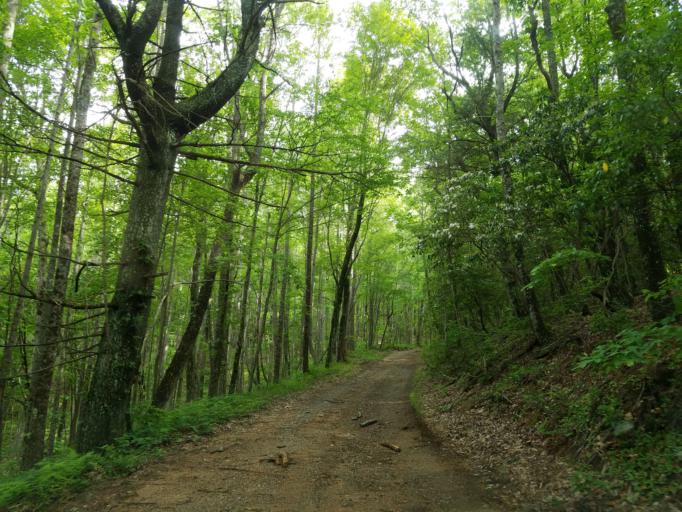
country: US
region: Georgia
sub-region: Union County
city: Blairsville
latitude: 34.7366
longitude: -84.0203
